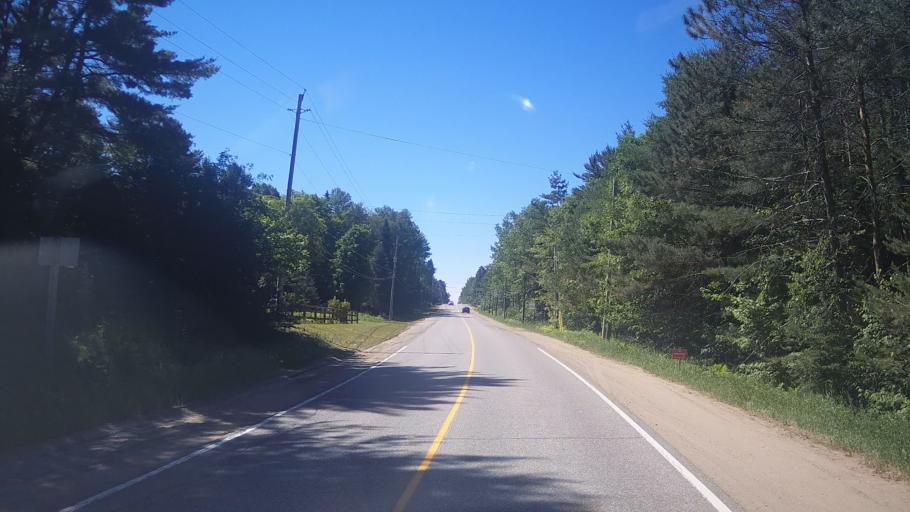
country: CA
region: Ontario
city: Huntsville
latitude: 45.3626
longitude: -79.2049
